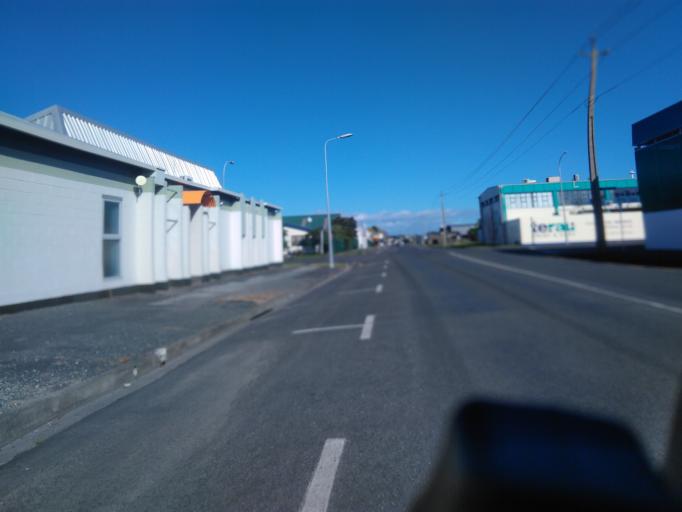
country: NZ
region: Gisborne
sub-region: Gisborne District
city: Gisborne
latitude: -38.6690
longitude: 178.0236
